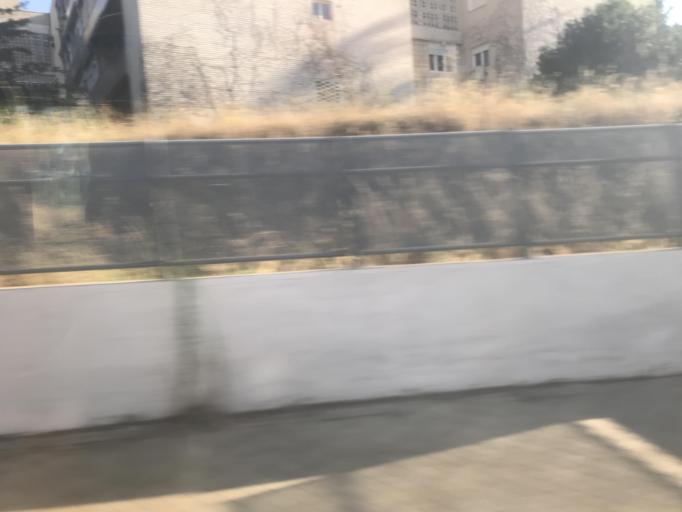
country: ES
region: Madrid
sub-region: Provincia de Madrid
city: Majadahonda
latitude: 40.4737
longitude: -3.8437
